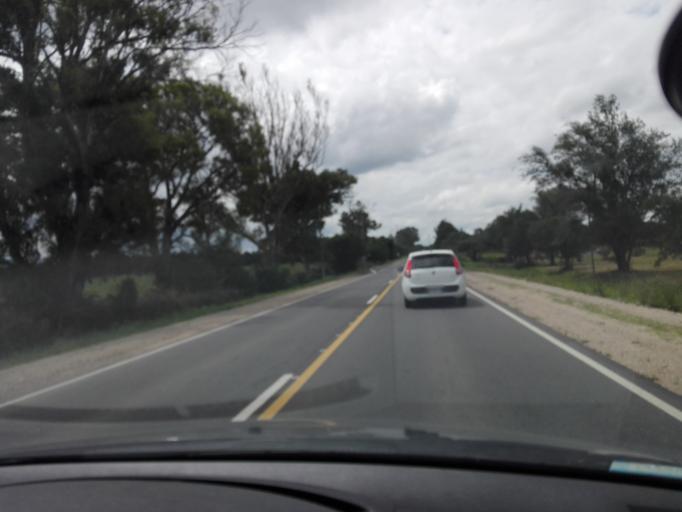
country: AR
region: Cordoba
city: Alta Gracia
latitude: -31.5990
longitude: -64.4518
